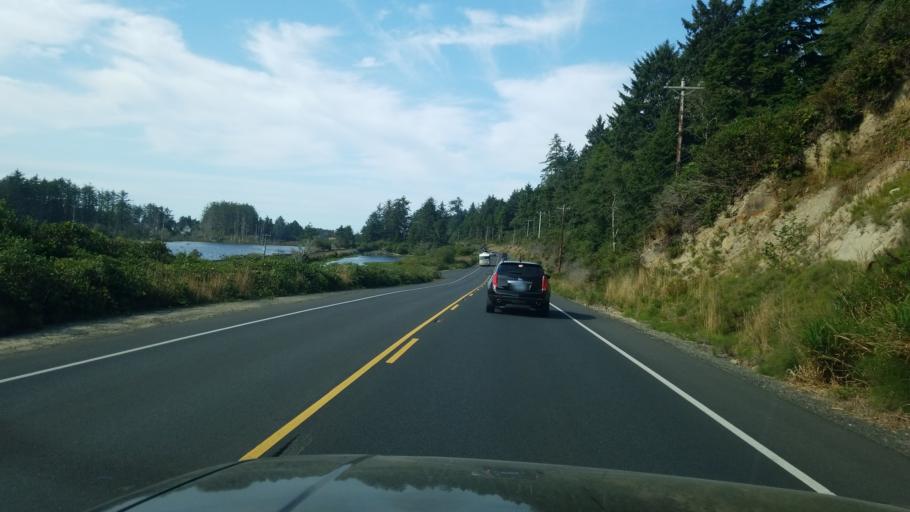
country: US
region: Oregon
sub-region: Tillamook County
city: Rockaway Beach
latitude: 45.5785
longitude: -123.9453
